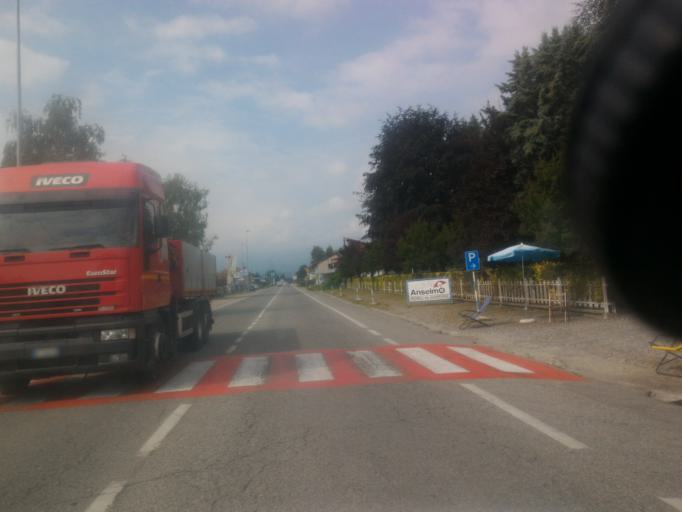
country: IT
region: Piedmont
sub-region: Provincia di Torino
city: Osasco
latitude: 44.8604
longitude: 7.3285
